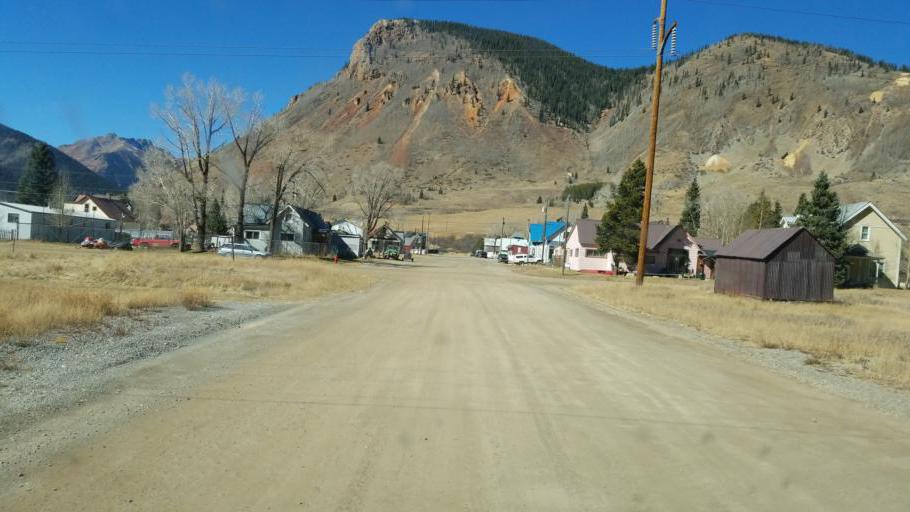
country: US
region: Colorado
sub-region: San Juan County
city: Silverton
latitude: 37.8069
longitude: -107.6656
